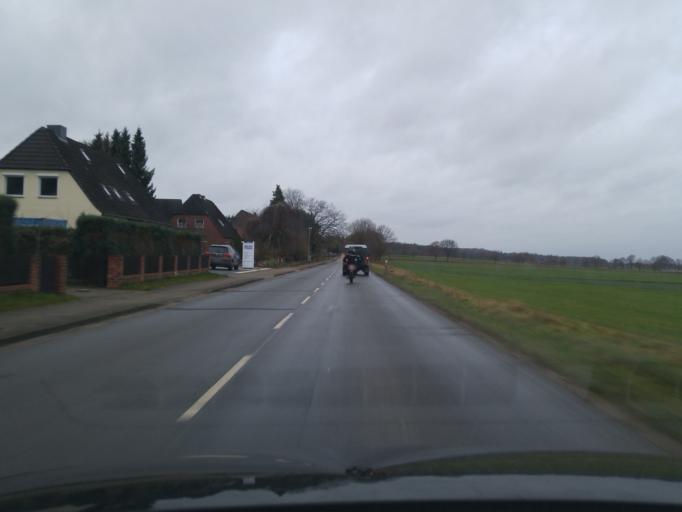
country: DE
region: Lower Saxony
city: Rullstorf
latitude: 53.2710
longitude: 10.5154
